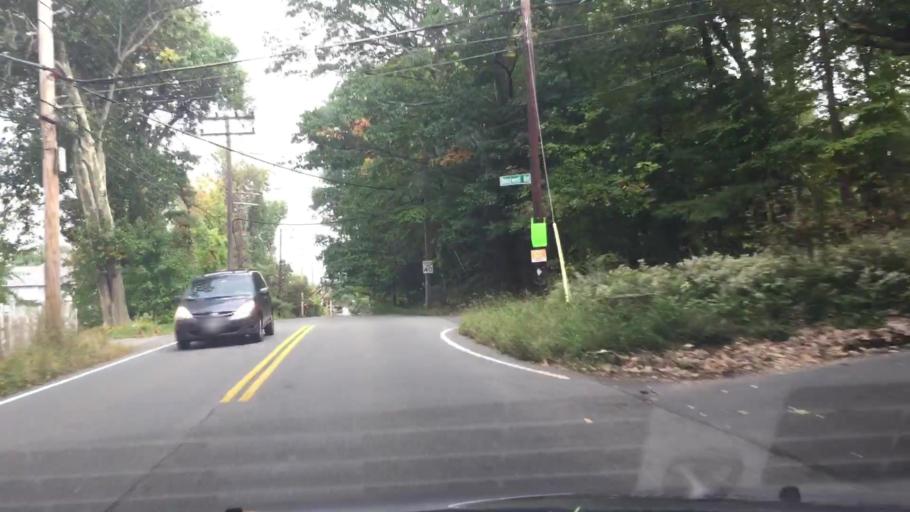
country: US
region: Massachusetts
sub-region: Middlesex County
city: Tewksbury
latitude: 42.6660
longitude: -71.2343
